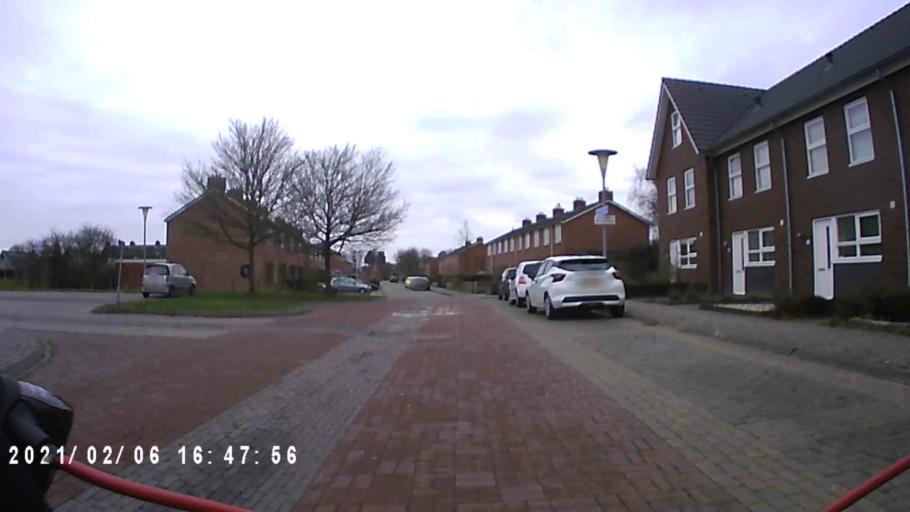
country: NL
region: Groningen
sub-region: Gemeente Appingedam
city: Appingedam
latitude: 53.4159
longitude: 6.7307
